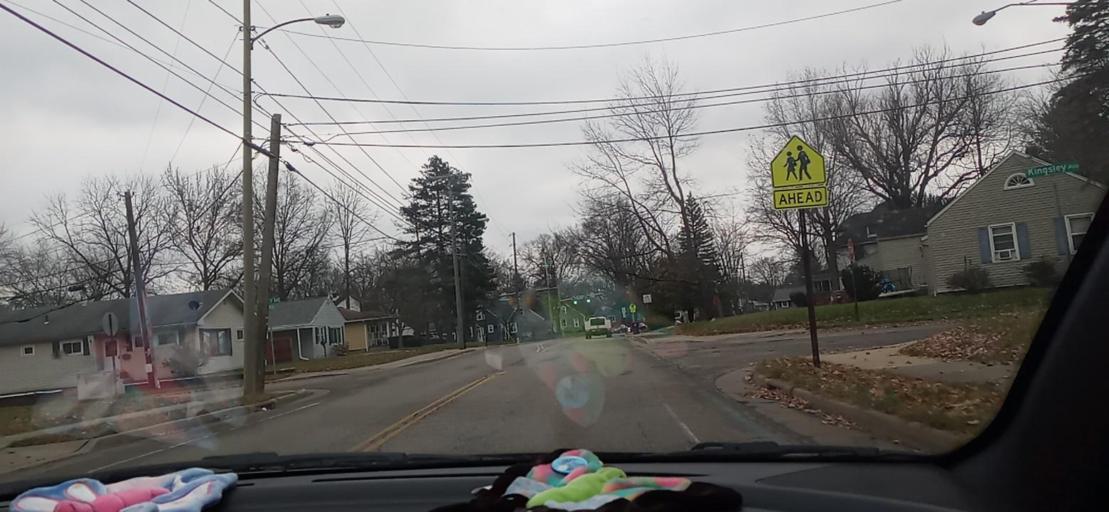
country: US
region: Ohio
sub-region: Summit County
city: Fairlawn
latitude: 41.1202
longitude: -81.5698
